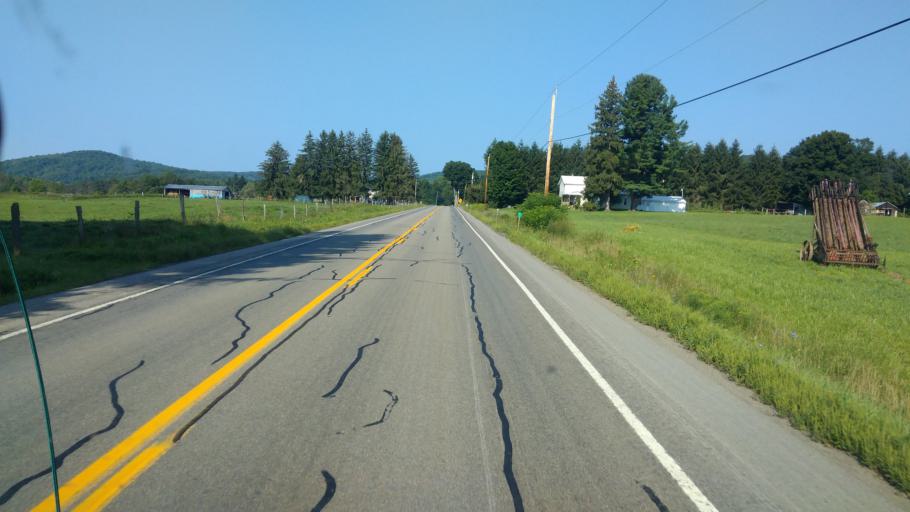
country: US
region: New York
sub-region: Allegany County
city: Friendship
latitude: 42.3046
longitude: -78.1728
